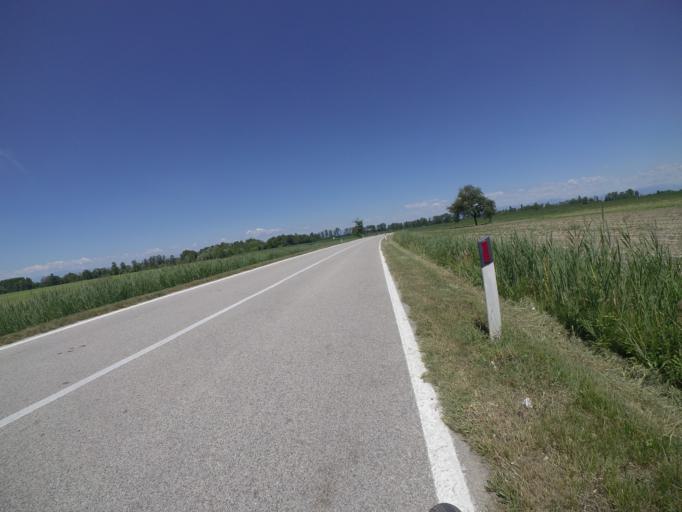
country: IT
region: Friuli Venezia Giulia
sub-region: Provincia di Udine
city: Bertiolo
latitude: 45.9076
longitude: 13.0812
